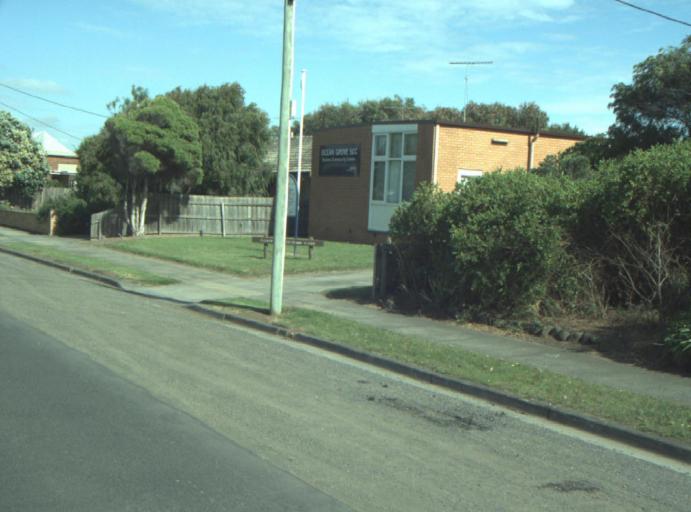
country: AU
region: Victoria
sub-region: Greater Geelong
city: Leopold
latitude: -38.2679
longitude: 144.5270
